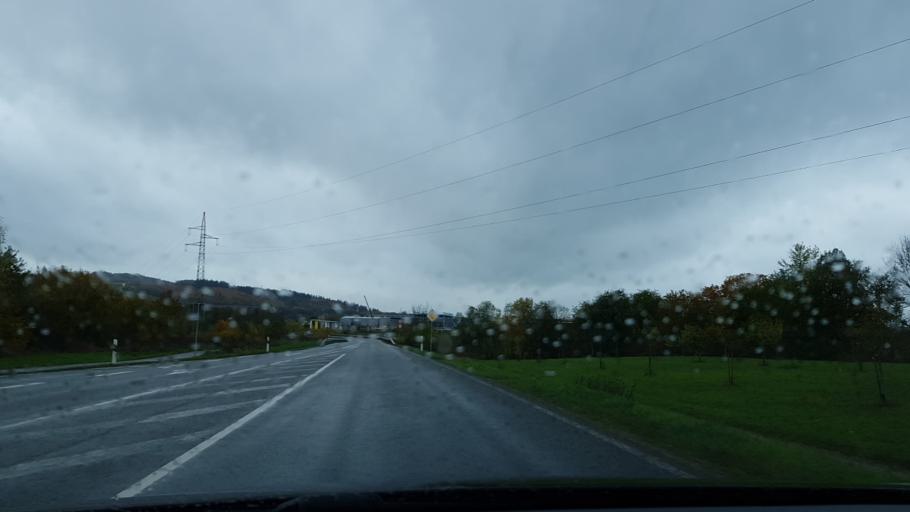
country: DE
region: Rheinland-Pfalz
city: Bekond
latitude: 49.8615
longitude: 6.8017
